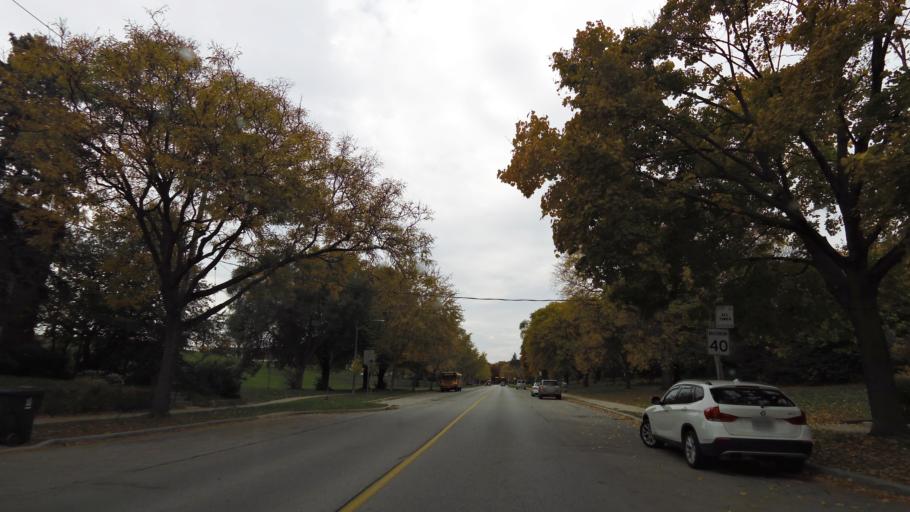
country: CA
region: Ontario
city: Etobicoke
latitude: 43.6648
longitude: -79.5236
